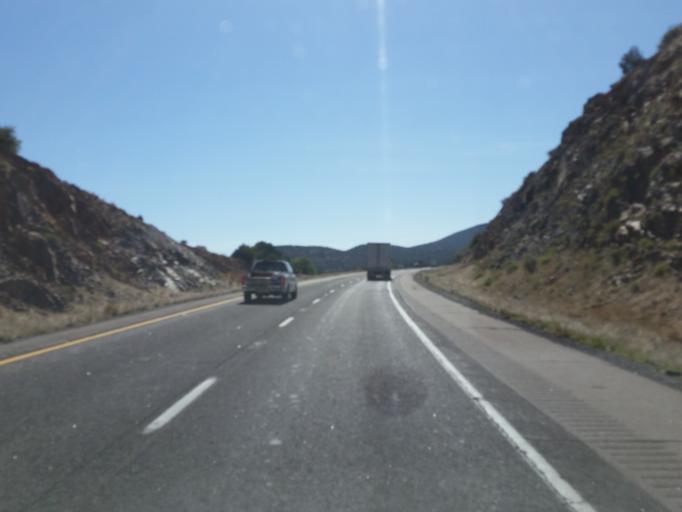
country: US
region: Arizona
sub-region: Mohave County
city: Peach Springs
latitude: 35.1810
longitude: -113.4657
